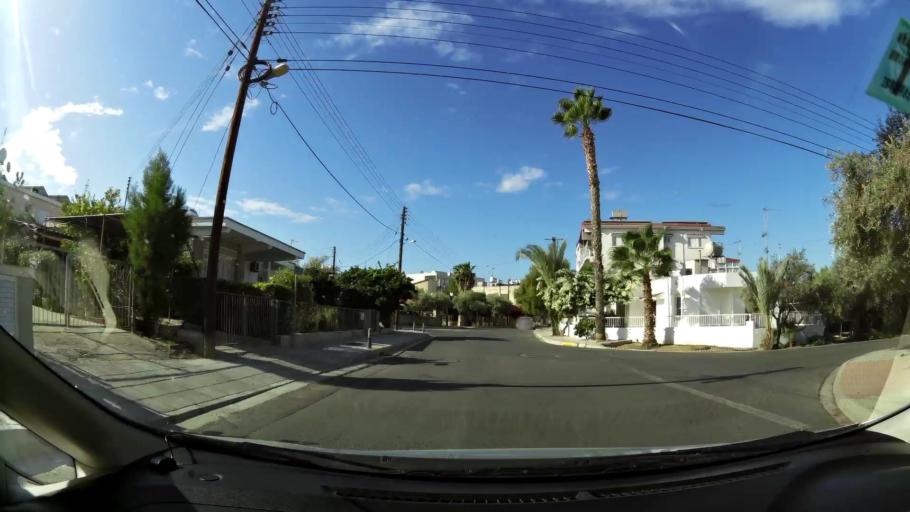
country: CY
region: Lefkosia
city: Nicosia
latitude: 35.1352
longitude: 33.3467
